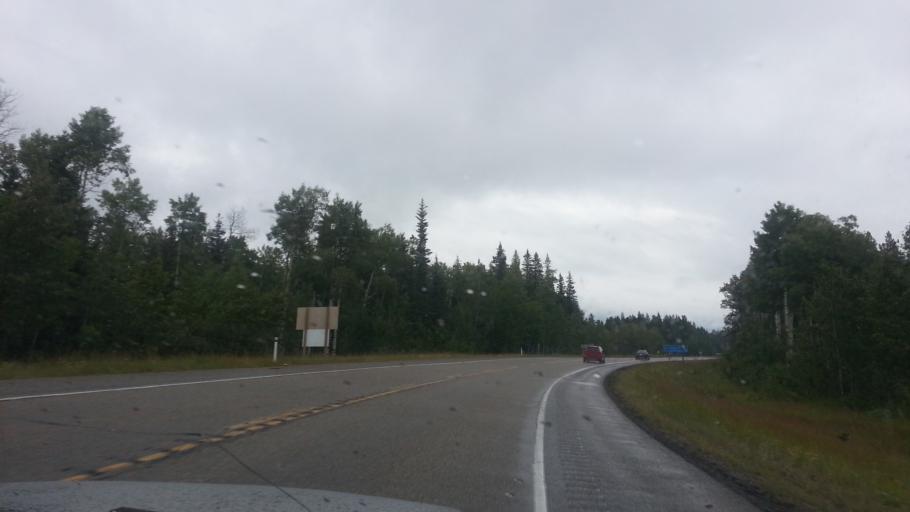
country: CA
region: Alberta
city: Cochrane
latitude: 50.9116
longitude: -114.6431
